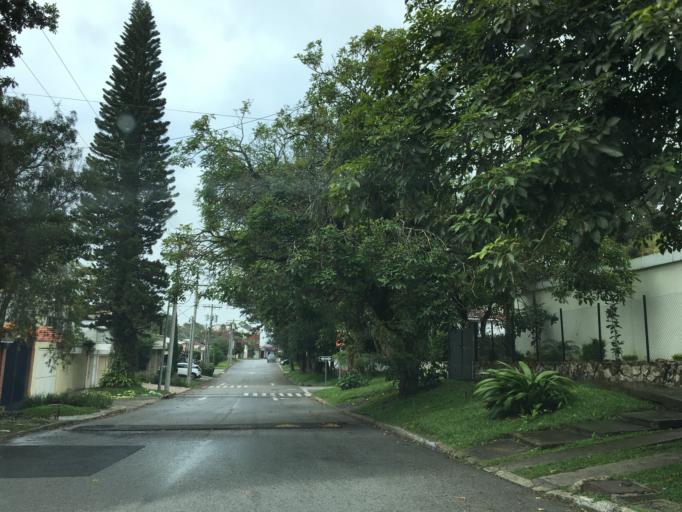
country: GT
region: Guatemala
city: Santa Catarina Pinula
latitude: 14.5894
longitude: -90.4956
